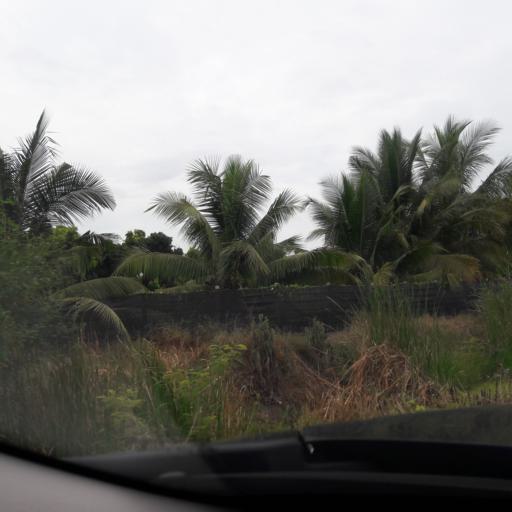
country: TH
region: Ratchaburi
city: Damnoen Saduak
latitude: 13.5763
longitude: 99.9442
